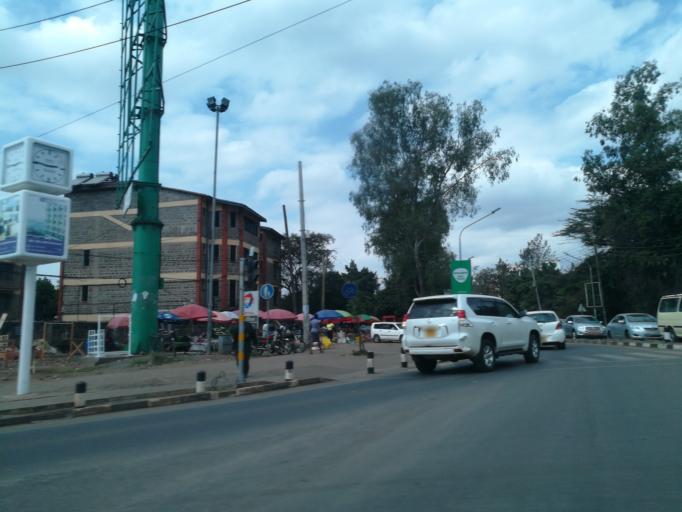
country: KE
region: Nairobi Area
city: Nairobi
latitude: -1.2853
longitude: 36.7882
